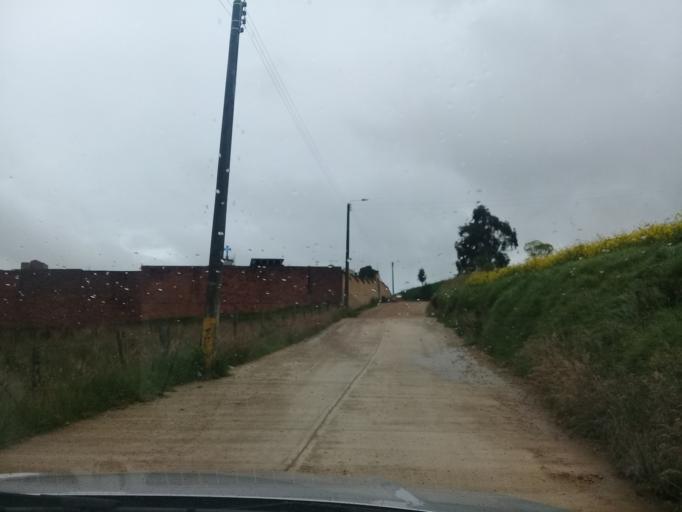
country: CO
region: Boyaca
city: Samaca
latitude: 5.4469
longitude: -73.4356
